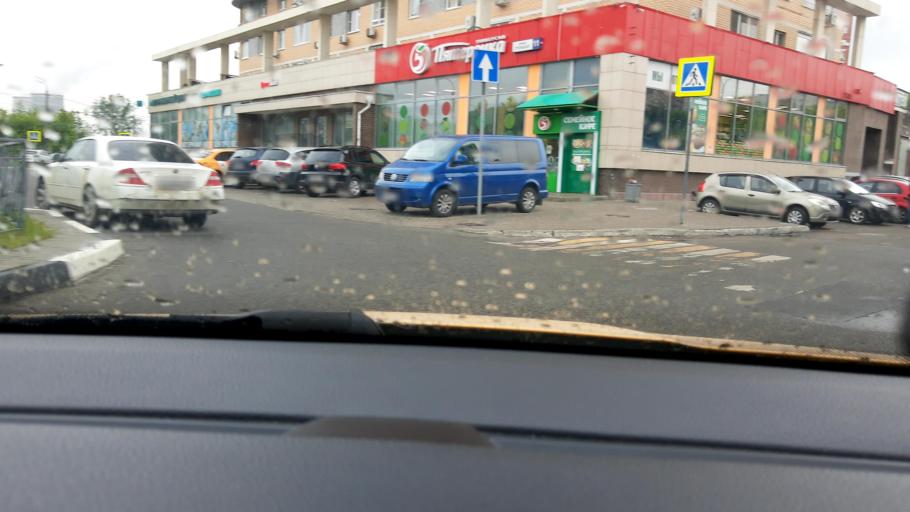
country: RU
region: Moscow
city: Vatutino
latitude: 55.9028
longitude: 37.6992
